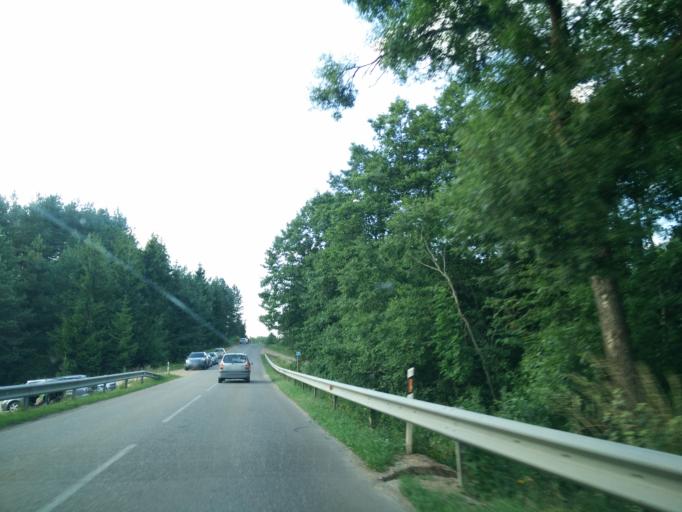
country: LT
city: Trakai
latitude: 54.6917
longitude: 24.9600
